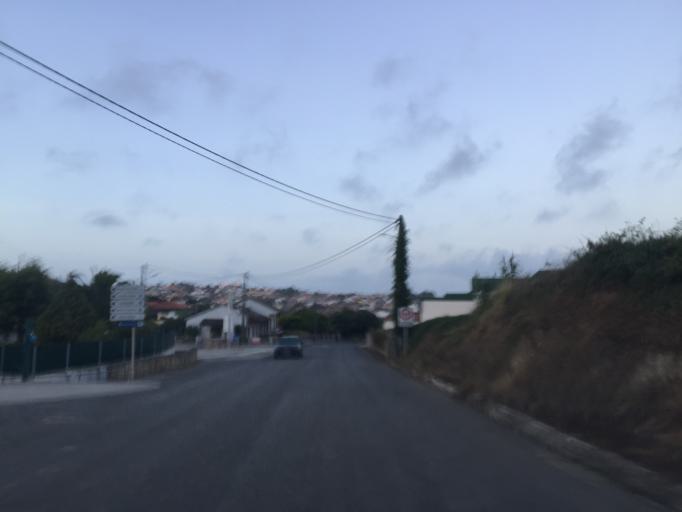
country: PT
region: Leiria
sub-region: Bombarral
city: Bombarral
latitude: 39.2843
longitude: -9.2202
